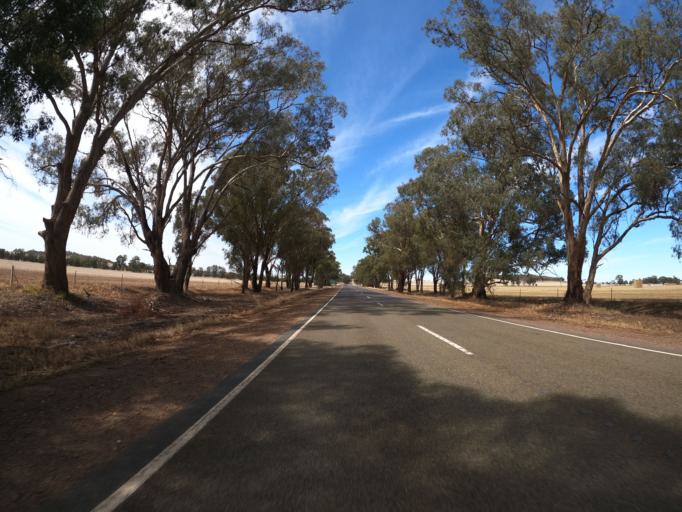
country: AU
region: Victoria
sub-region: Benalla
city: Benalla
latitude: -36.3145
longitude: 145.9583
